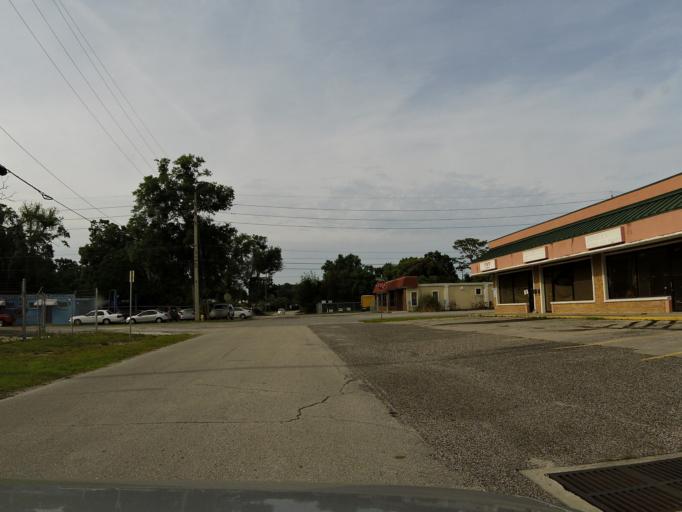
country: US
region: Florida
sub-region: Duval County
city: Jacksonville
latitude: 30.3343
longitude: -81.5978
